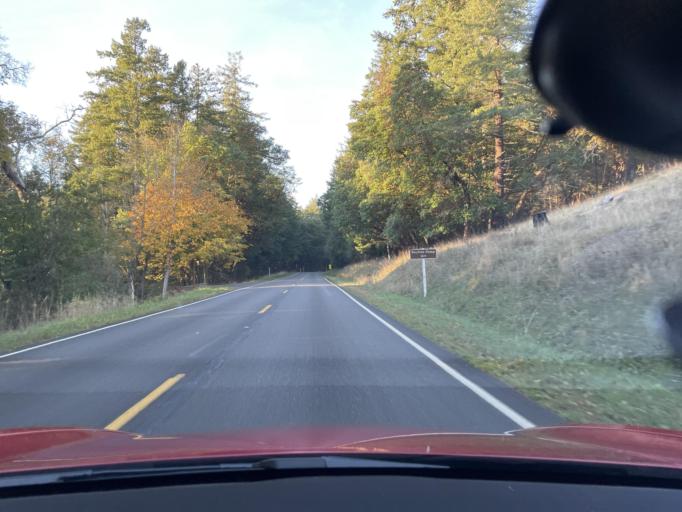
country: US
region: Washington
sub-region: San Juan County
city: Friday Harbor
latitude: 48.5818
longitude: -123.1442
